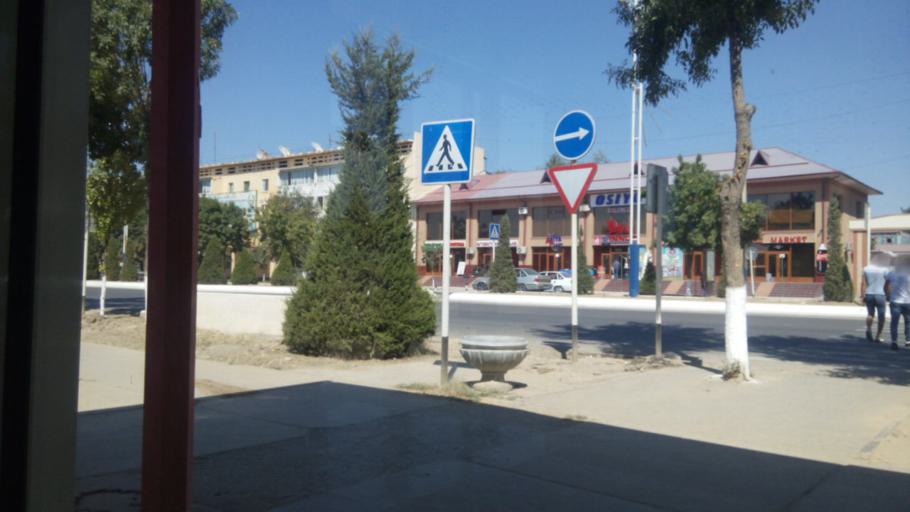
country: UZ
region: Sirdaryo
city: Guliston
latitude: 40.5024
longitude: 68.7729
